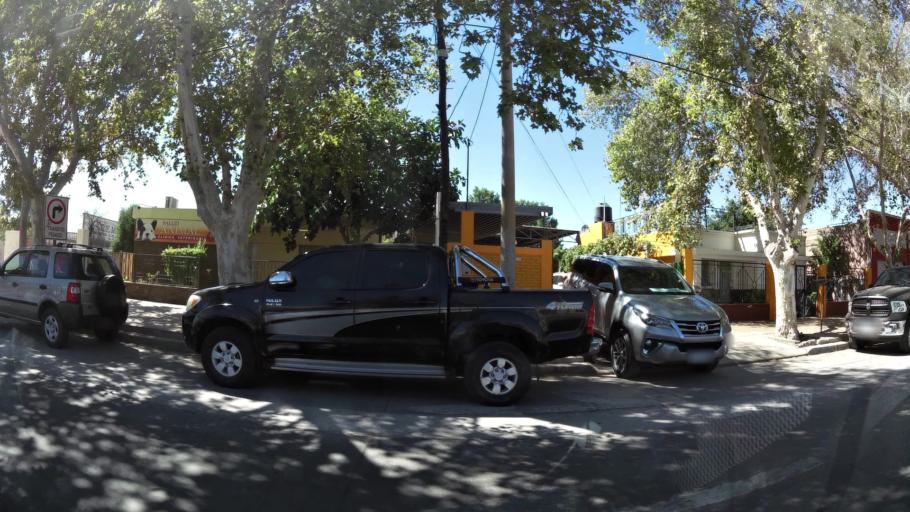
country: AR
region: San Juan
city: Villa Krause
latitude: -31.5595
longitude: -68.5240
